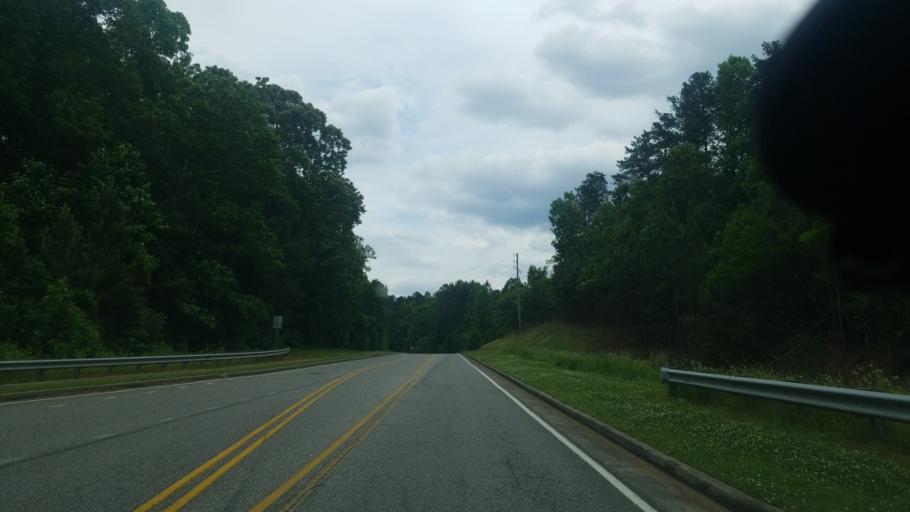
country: US
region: Georgia
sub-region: Forsyth County
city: Cumming
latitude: 34.1731
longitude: -84.1370
